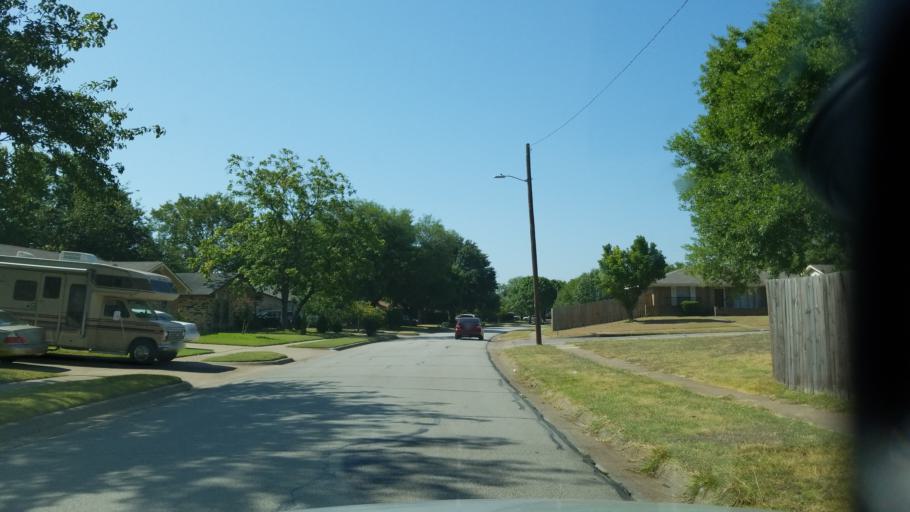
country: US
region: Texas
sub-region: Dallas County
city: Duncanville
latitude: 32.6376
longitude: -96.9004
